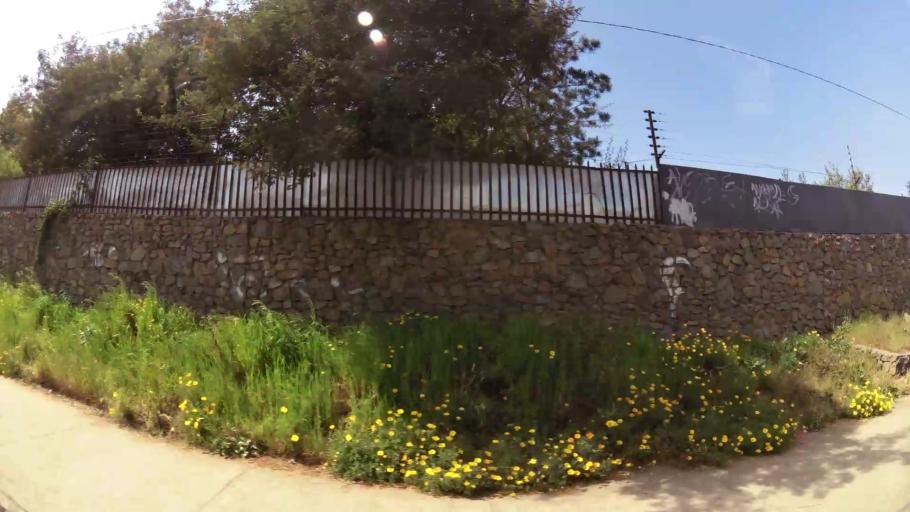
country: CL
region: Santiago Metropolitan
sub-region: Provincia de Santiago
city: Villa Presidente Frei, Nunoa, Santiago, Chile
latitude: -33.4759
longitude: -70.5250
